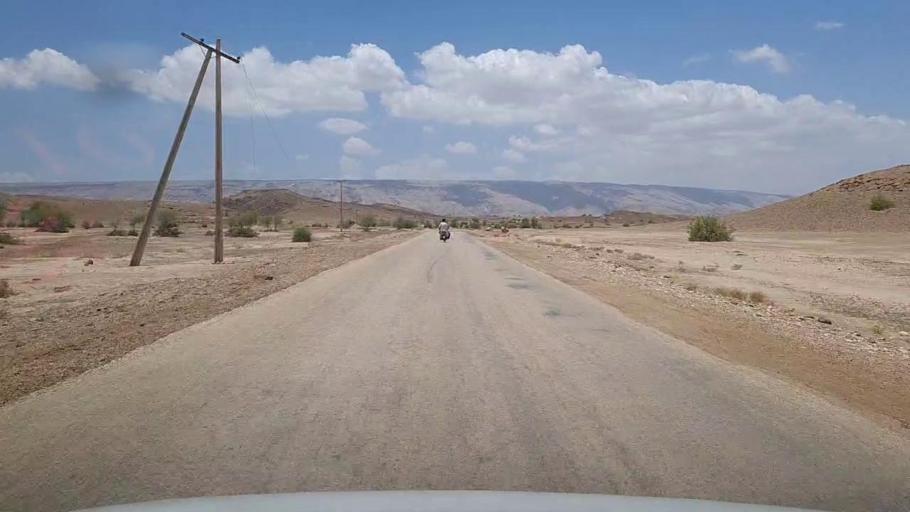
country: PK
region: Sindh
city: Bhan
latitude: 26.3169
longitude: 67.5677
